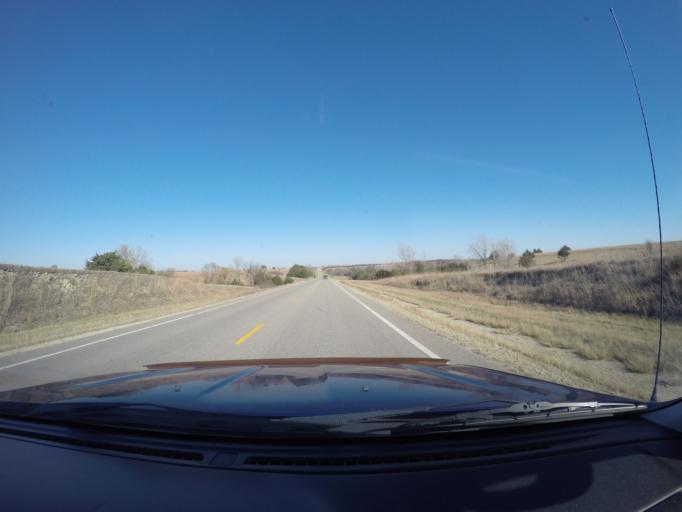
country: US
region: Kansas
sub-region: Riley County
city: Ogden
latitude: 39.3153
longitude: -96.7557
